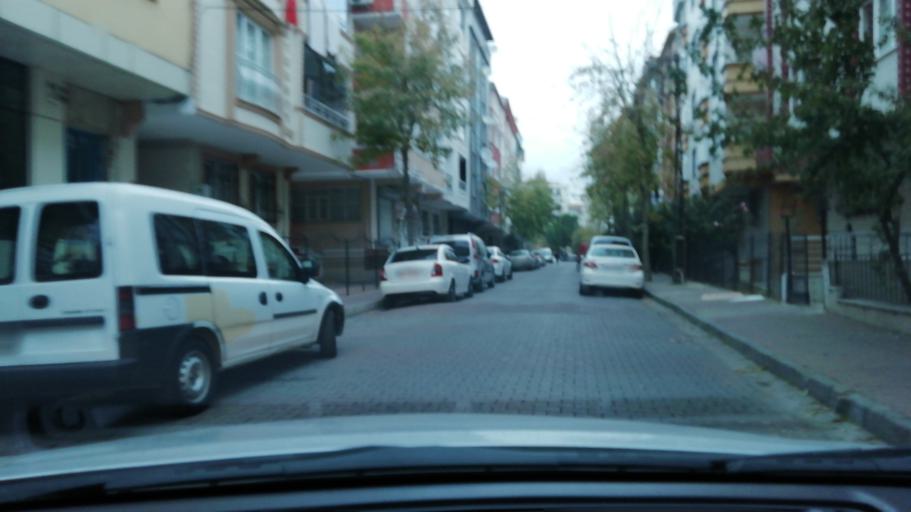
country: TR
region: Istanbul
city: Bagcilar
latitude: 41.0205
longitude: 28.8300
